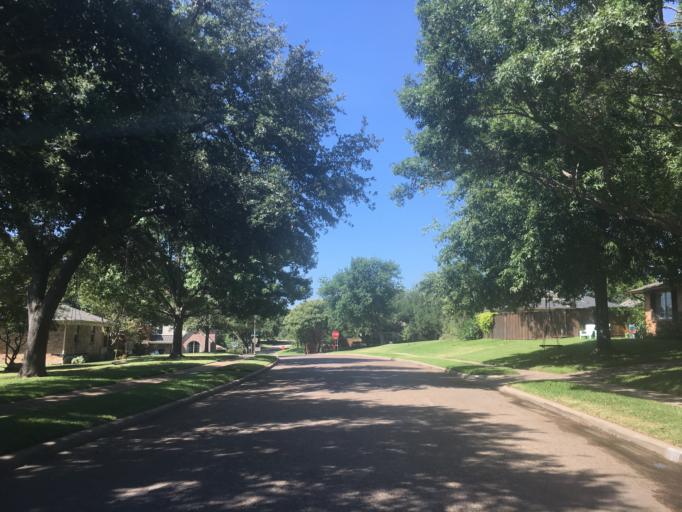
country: US
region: Texas
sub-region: Dallas County
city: Richardson
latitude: 32.8723
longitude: -96.7201
